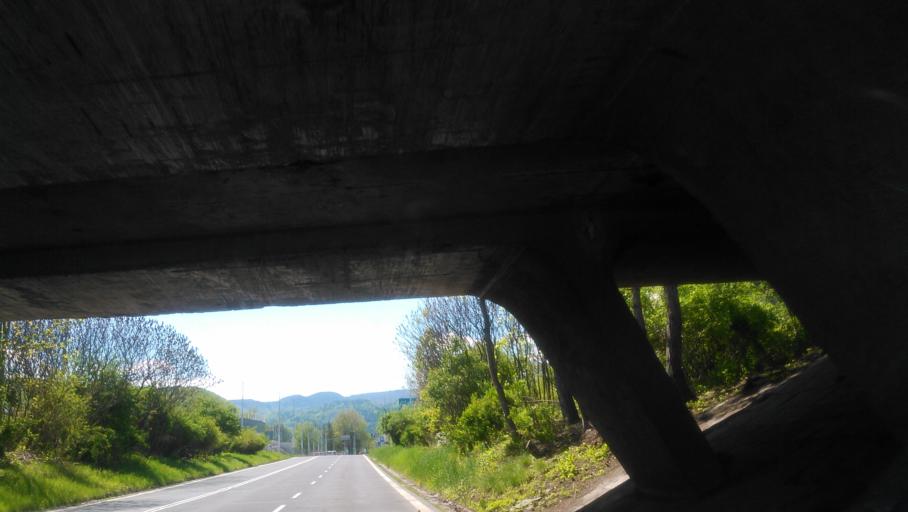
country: SK
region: Banskobystricky
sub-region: Okres Banska Bystrica
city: Banska Bystrica
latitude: 48.7362
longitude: 19.1628
